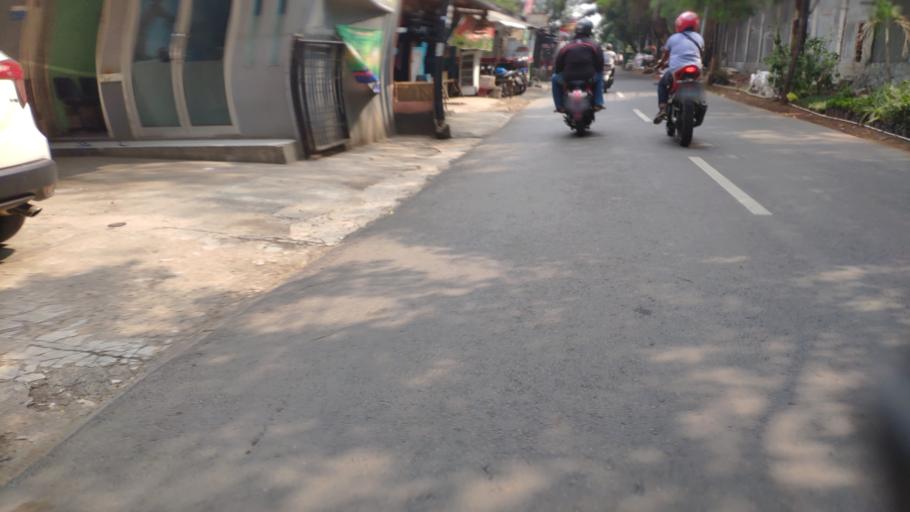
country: ID
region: West Java
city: Depok
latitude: -6.3162
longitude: 106.8252
